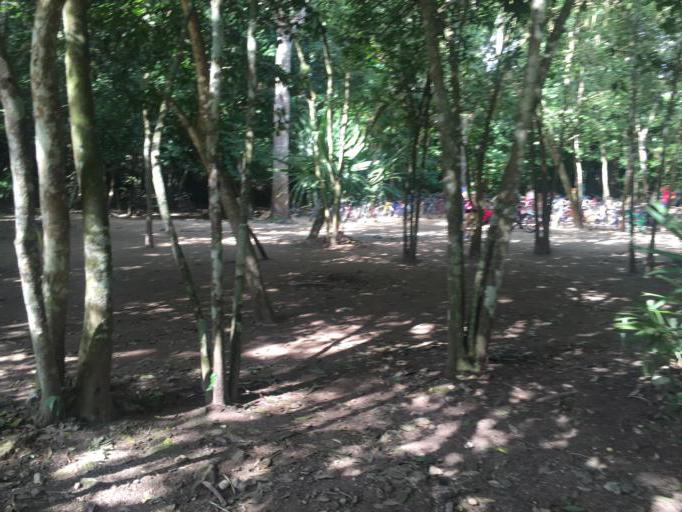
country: MX
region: Quintana Roo
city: Coba
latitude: 20.4904
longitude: -87.7319
